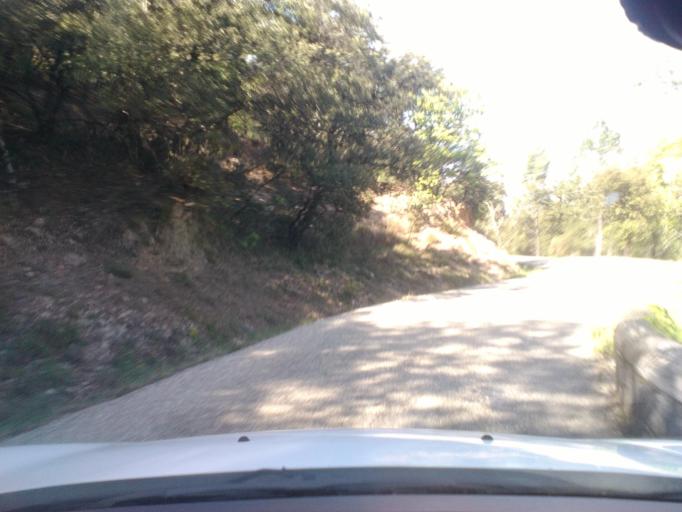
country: FR
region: Languedoc-Roussillon
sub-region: Departement du Gard
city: Lasalle
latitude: 44.0158
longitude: 3.8736
